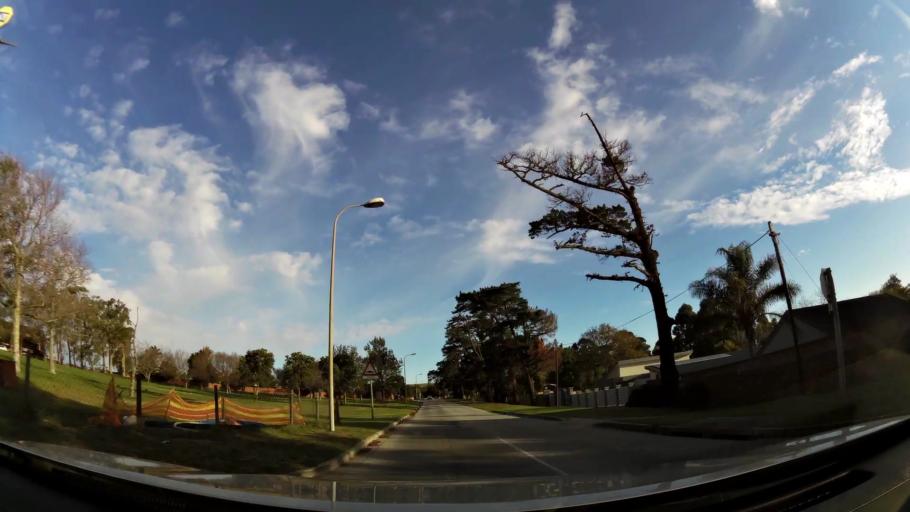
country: ZA
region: Eastern Cape
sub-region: Nelson Mandela Bay Metropolitan Municipality
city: Port Elizabeth
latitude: -33.9652
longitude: 25.5071
